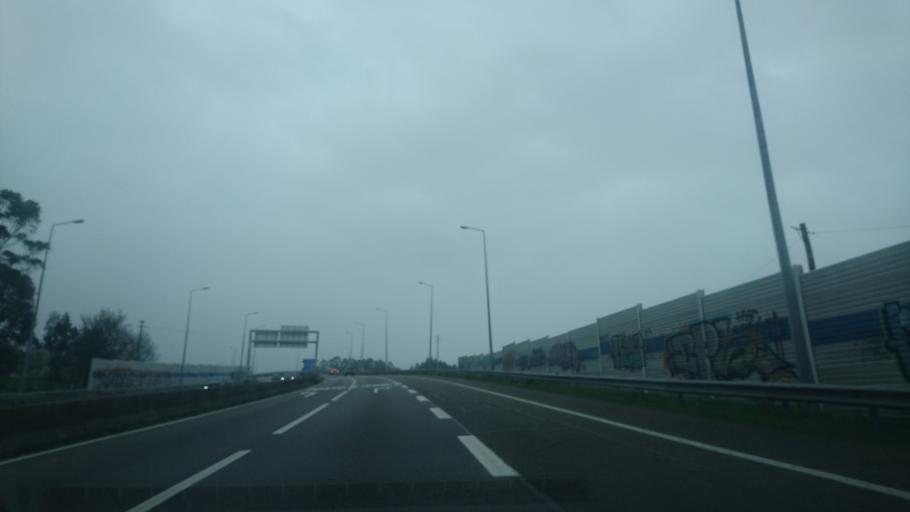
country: PT
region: Porto
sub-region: Vila Nova de Gaia
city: Gulpilhares
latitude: 41.0834
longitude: -8.6312
